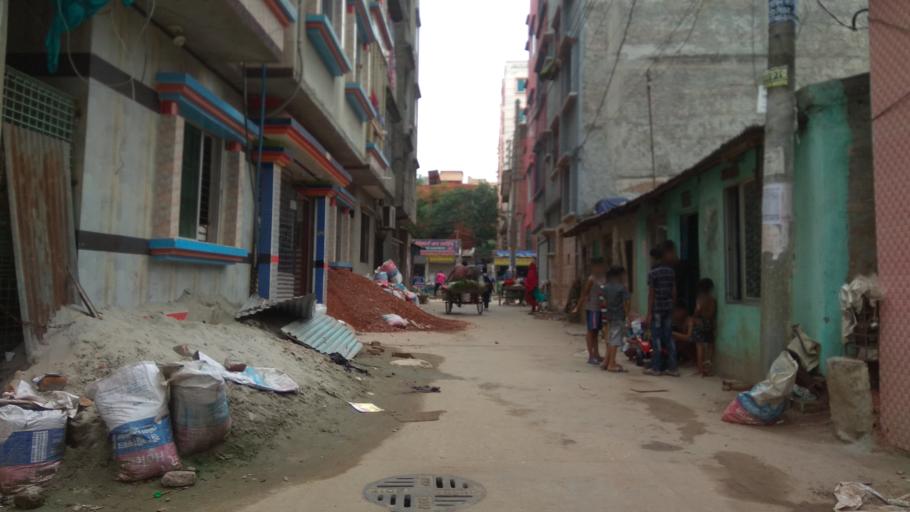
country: BD
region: Dhaka
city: Tungi
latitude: 23.8228
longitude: 90.3565
